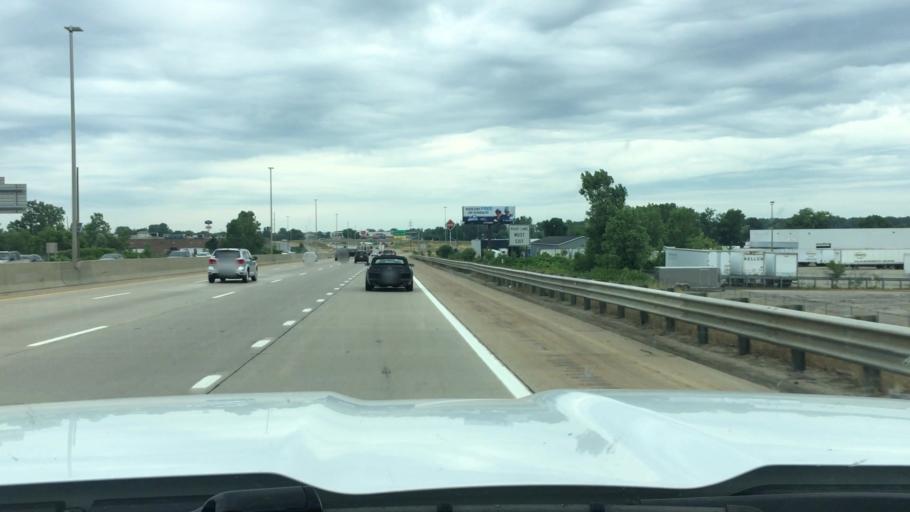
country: US
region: Michigan
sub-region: Kent County
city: Cutlerville
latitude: 42.8592
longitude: -85.6789
